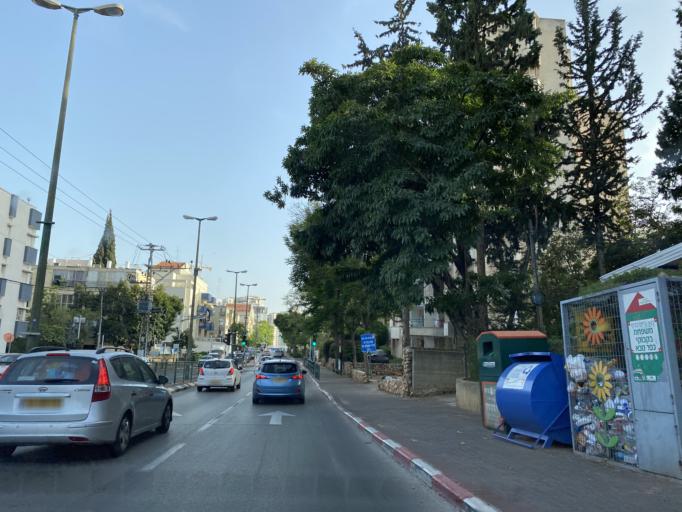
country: IL
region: Central District
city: Kfar Saba
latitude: 32.1744
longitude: 34.9020
